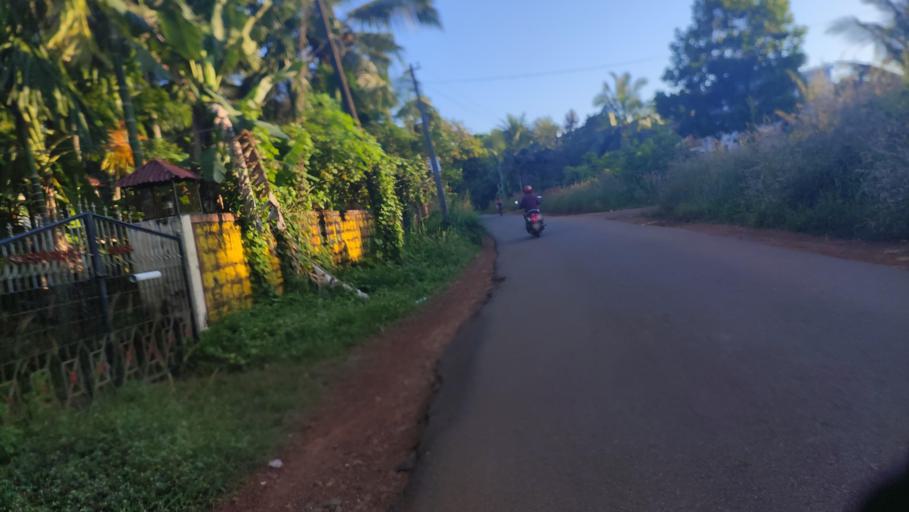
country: IN
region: Kerala
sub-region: Kasaragod District
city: Kannangad
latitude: 12.4137
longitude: 75.0950
